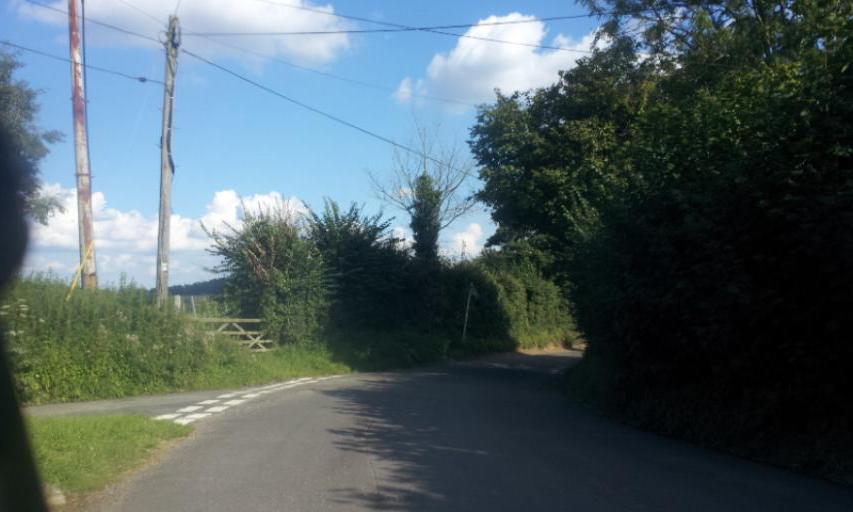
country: GB
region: England
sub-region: Kent
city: Hadlow
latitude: 51.2502
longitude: 0.3555
